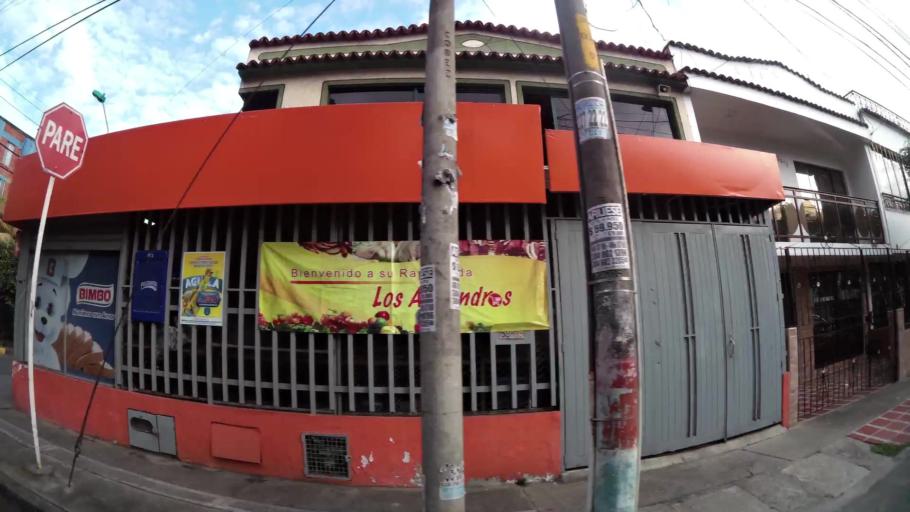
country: CO
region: Valle del Cauca
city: Cali
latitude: 3.4731
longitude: -76.4969
